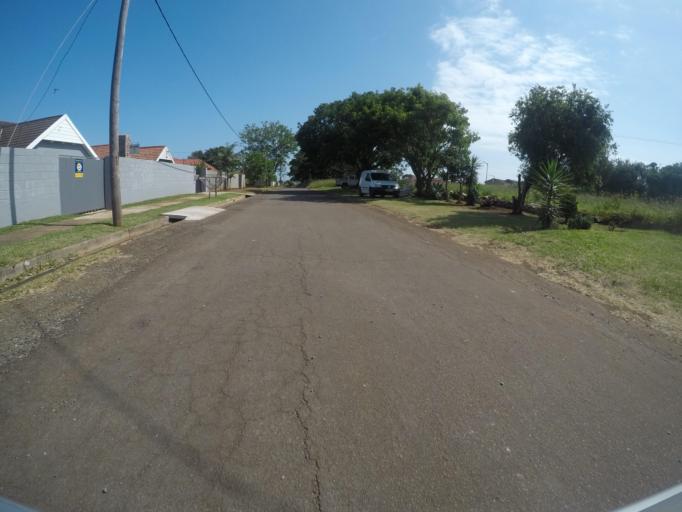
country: ZA
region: Eastern Cape
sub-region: Buffalo City Metropolitan Municipality
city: East London
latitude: -32.9683
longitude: 27.8755
